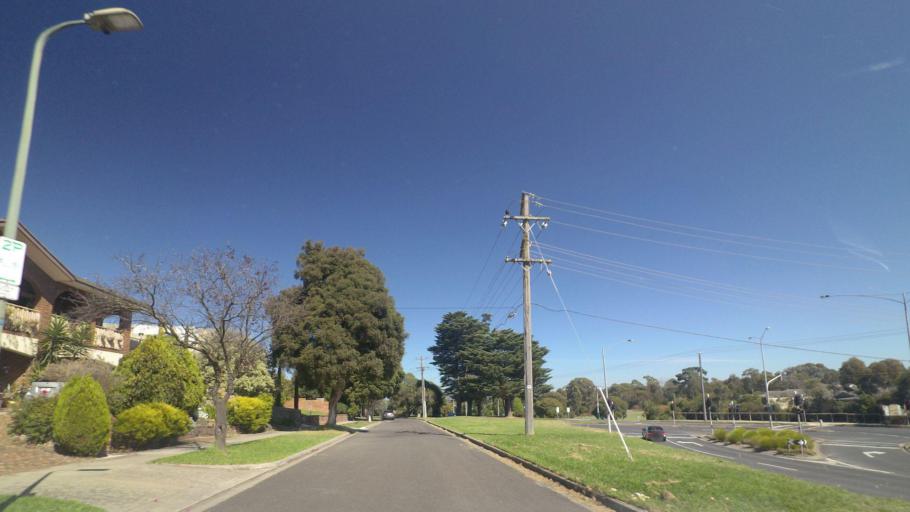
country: AU
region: Victoria
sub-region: Manningham
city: Donvale
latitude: -37.7776
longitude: 145.1648
